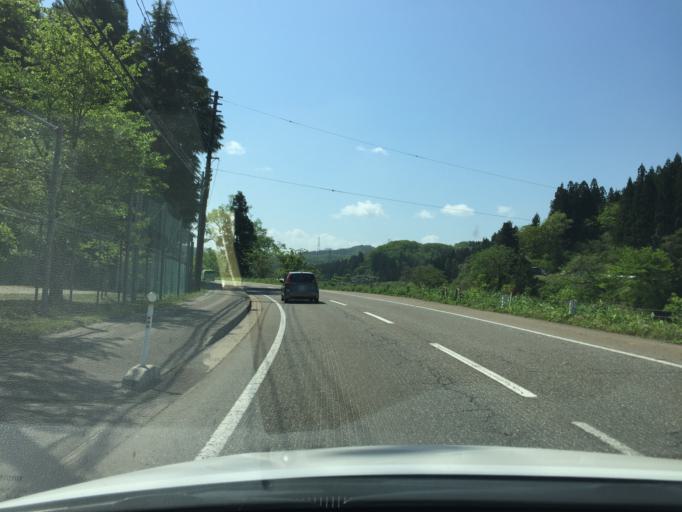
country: JP
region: Niigata
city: Kamo
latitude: 37.6135
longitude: 139.1022
